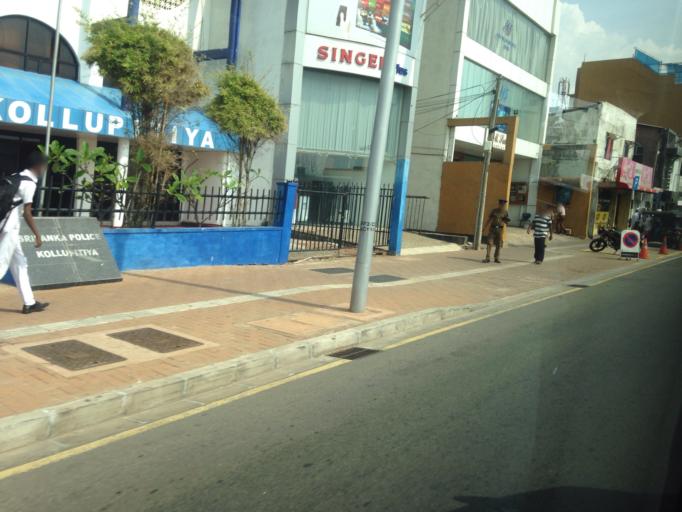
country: LK
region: Western
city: Colombo
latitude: 6.9142
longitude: 79.8488
